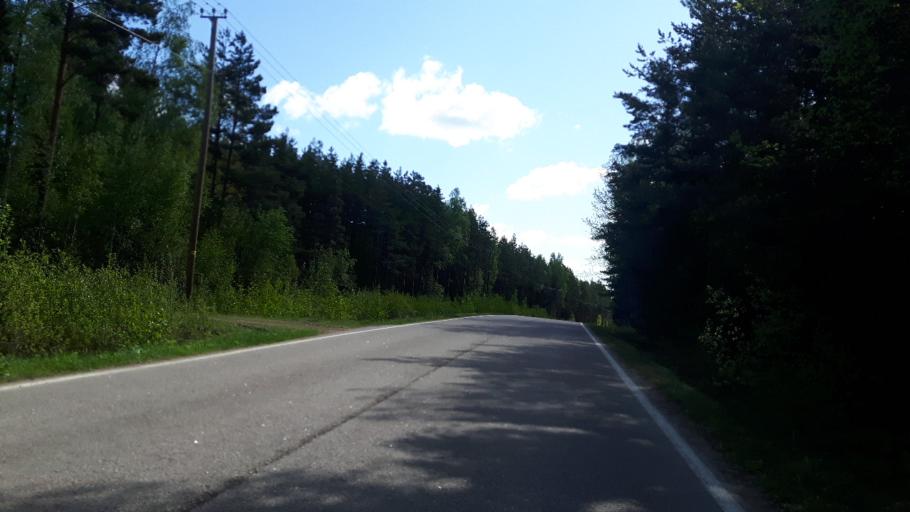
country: FI
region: Kymenlaakso
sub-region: Kotka-Hamina
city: Hamina
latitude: 60.5271
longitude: 27.2517
